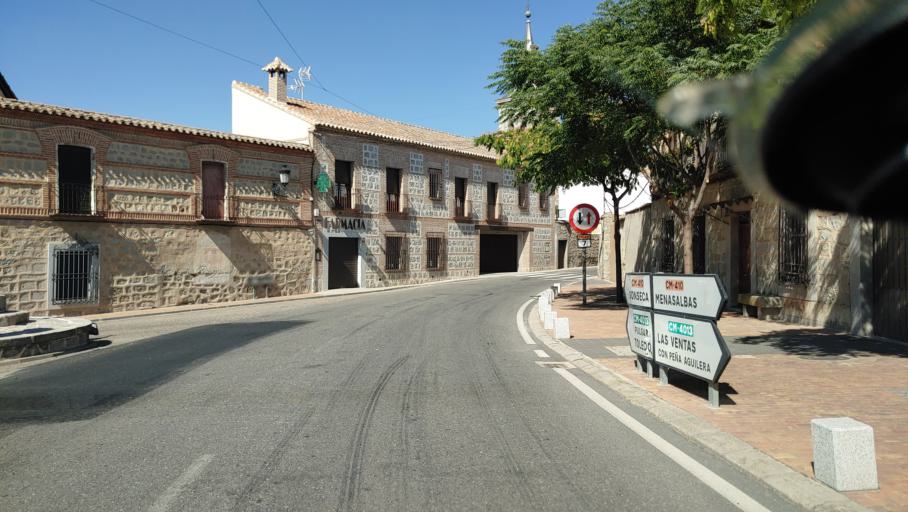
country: ES
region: Castille-La Mancha
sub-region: Province of Toledo
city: Cuerva
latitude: 39.6632
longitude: -4.2126
